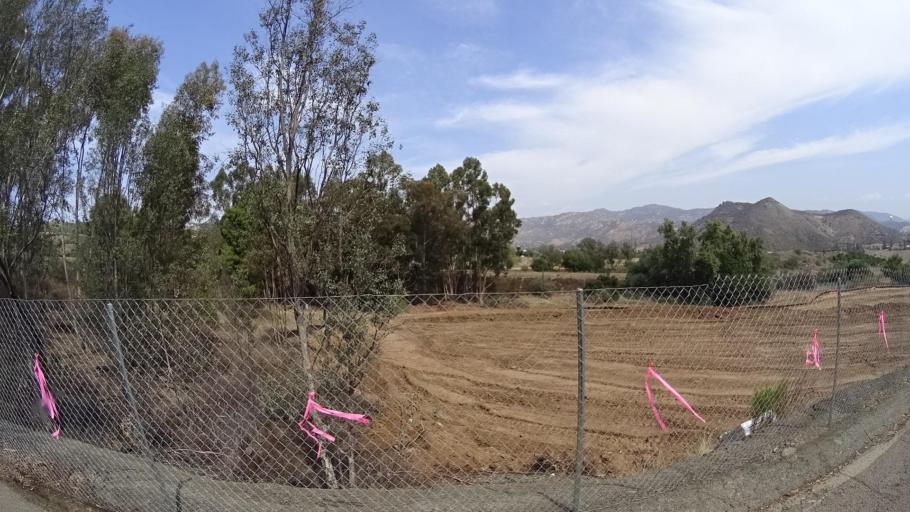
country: US
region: California
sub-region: San Diego County
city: Escondido
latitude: 33.0973
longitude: -117.0282
